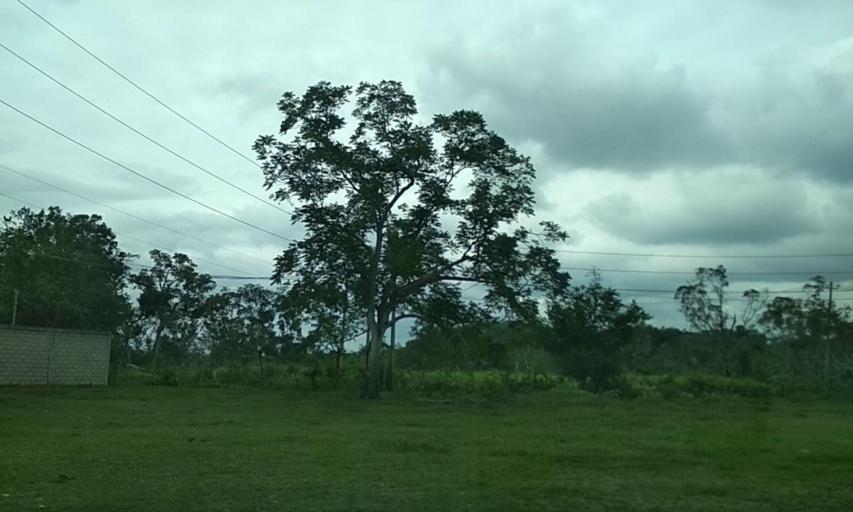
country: MX
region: Veracruz
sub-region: Papantla
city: El Chote
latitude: 20.3949
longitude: -97.3372
